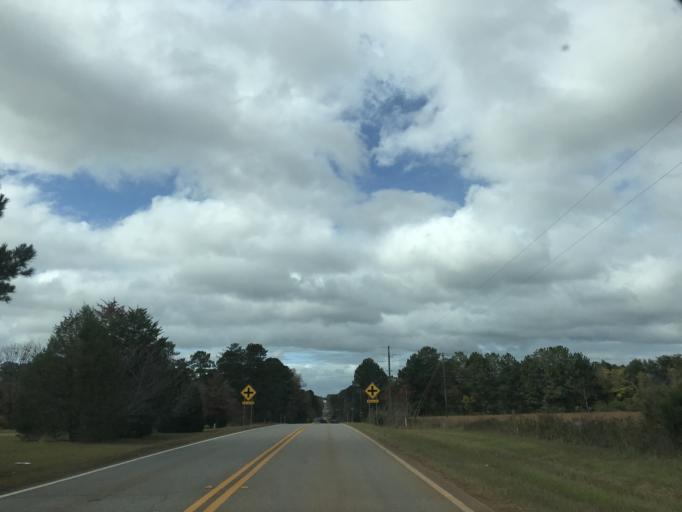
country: US
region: Georgia
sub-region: Jones County
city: Gray
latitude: 32.9796
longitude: -83.5073
